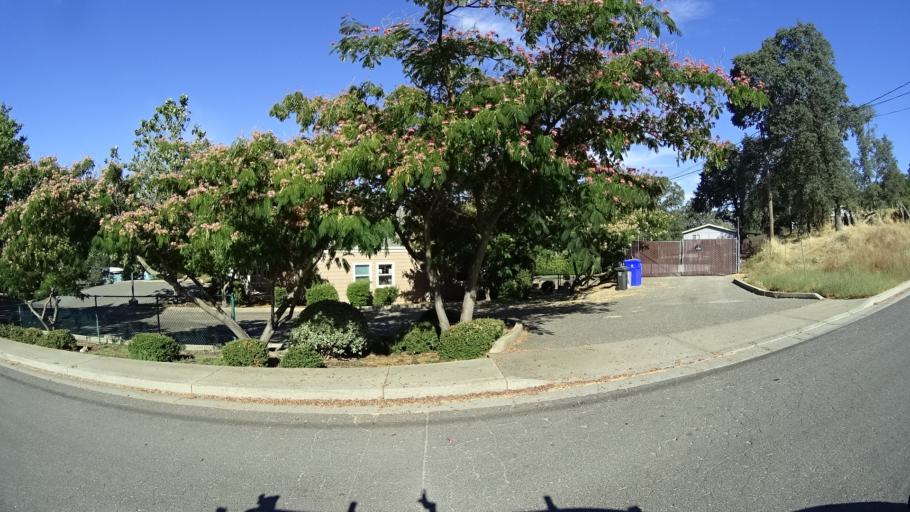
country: US
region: California
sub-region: Calaveras County
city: San Andreas
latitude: 38.1907
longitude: -120.6621
